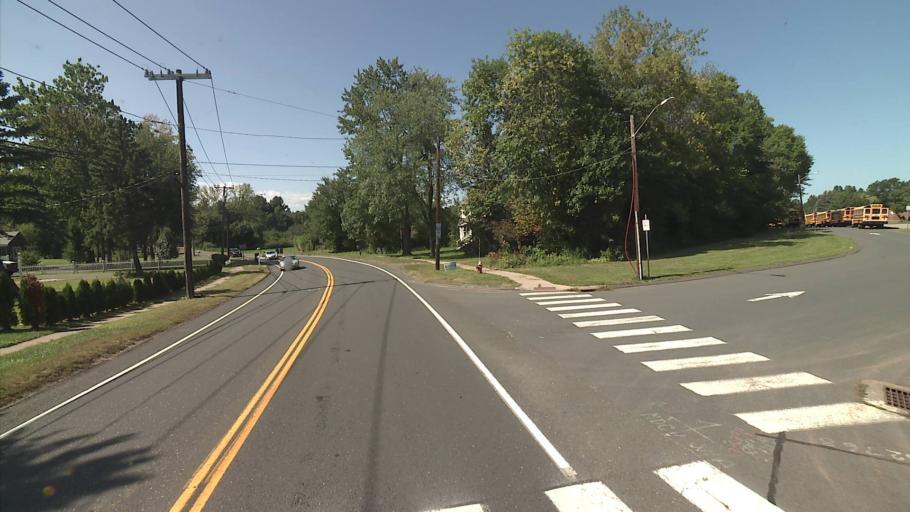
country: US
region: Connecticut
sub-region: Hartford County
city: Blue Hills
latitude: 41.8234
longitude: -72.7183
